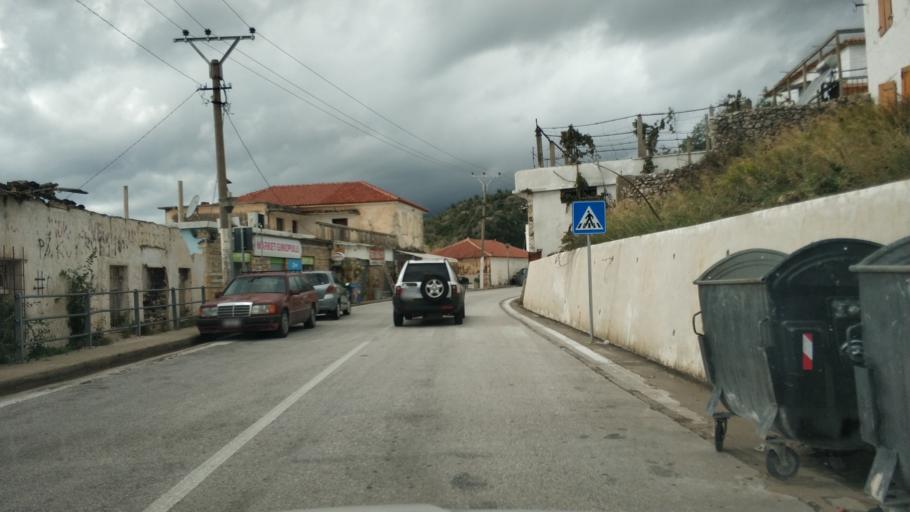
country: AL
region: Vlore
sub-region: Rrethi i Vlores
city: Vranisht
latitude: 40.1513
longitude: 19.6390
